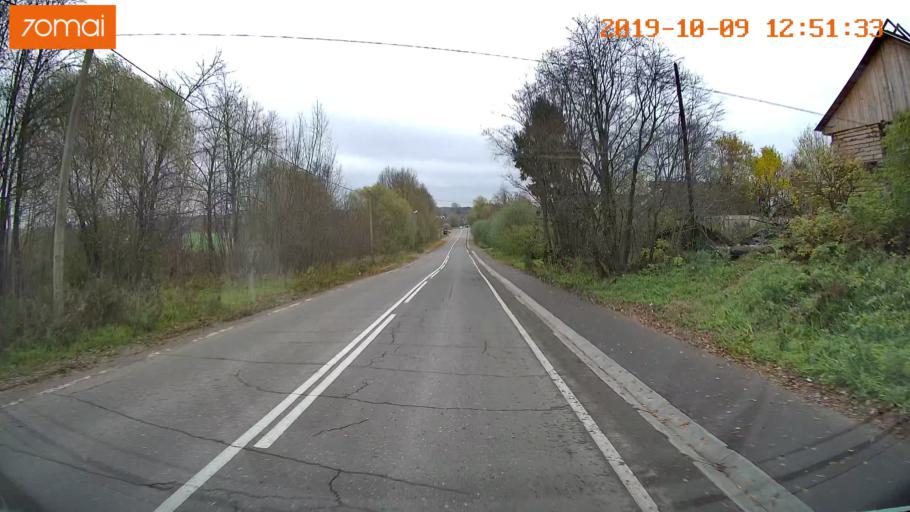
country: RU
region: Jaroslavl
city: Prechistoye
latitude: 58.4190
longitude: 40.3431
